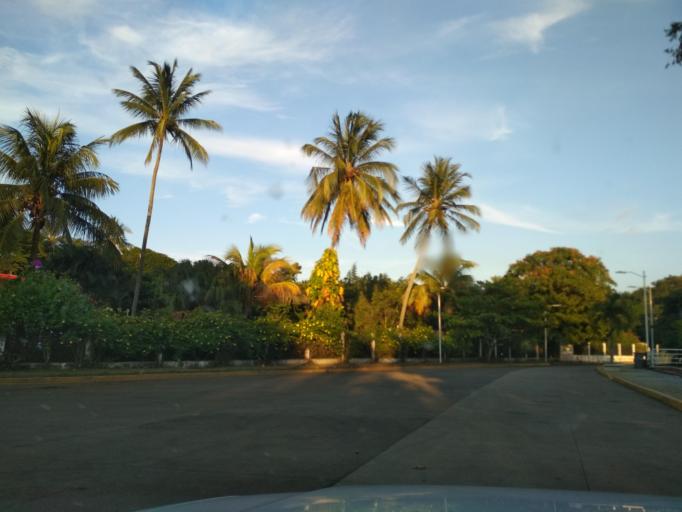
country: MX
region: Veracruz
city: Catemaco
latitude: 18.4170
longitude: -95.1063
